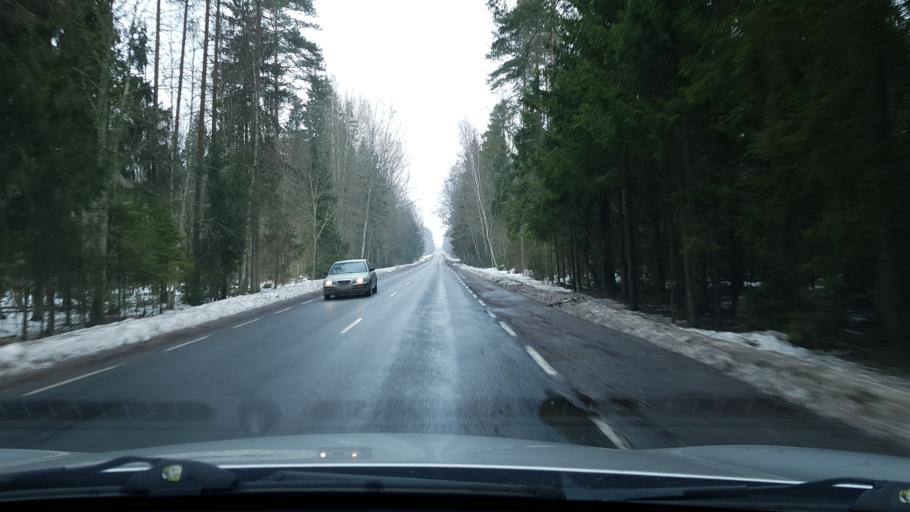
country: EE
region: Valgamaa
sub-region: Torva linn
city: Torva
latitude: 58.1723
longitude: 25.9627
